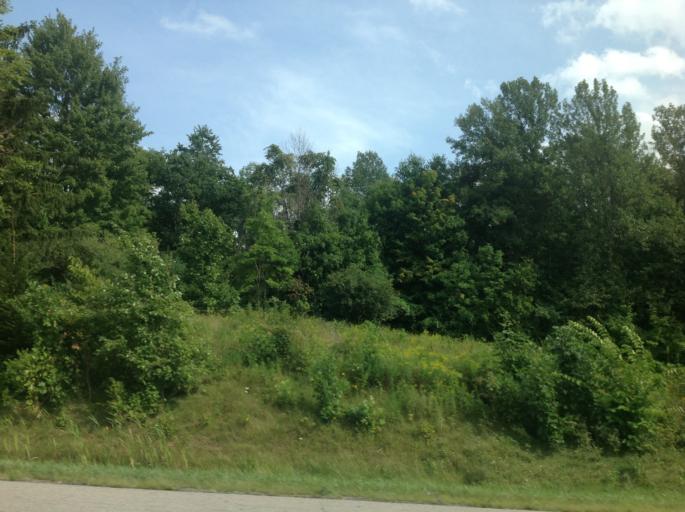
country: US
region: Ohio
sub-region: Richland County
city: Lincoln Heights
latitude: 40.7222
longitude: -82.4794
